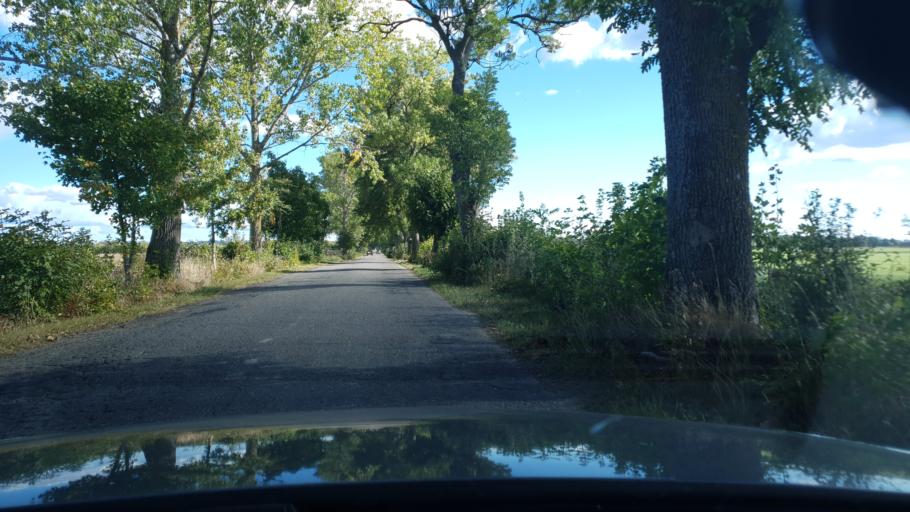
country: PL
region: Pomeranian Voivodeship
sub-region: Powiat pucki
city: Zelistrzewo
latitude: 54.6876
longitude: 18.4396
